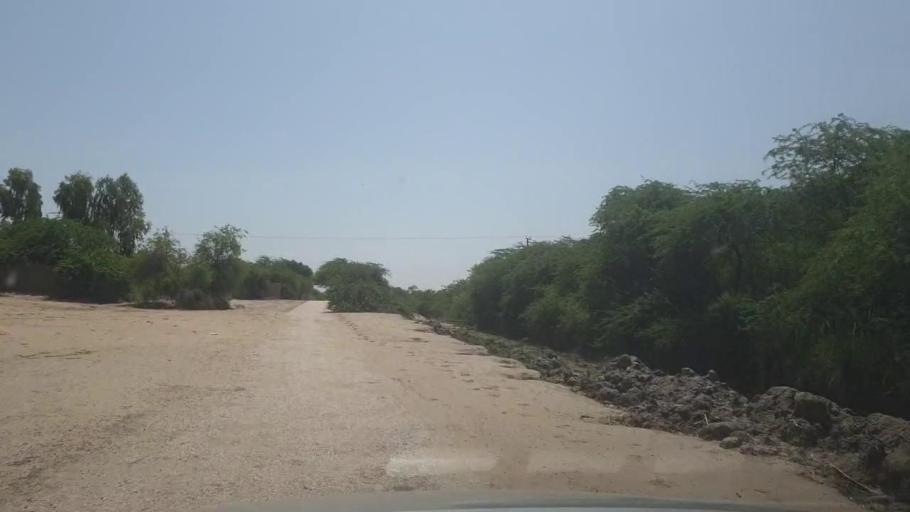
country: PK
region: Sindh
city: Khairpur
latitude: 27.3506
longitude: 69.0624
